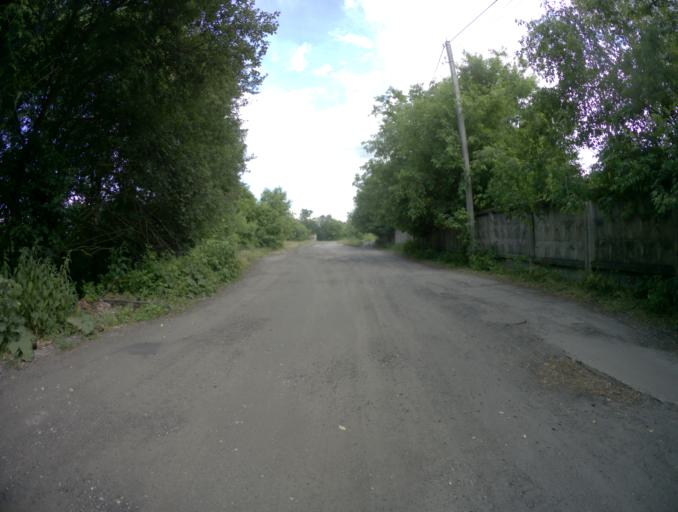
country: RU
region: Nizjnij Novgorod
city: Frolishchi
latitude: 56.4248
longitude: 42.6432
